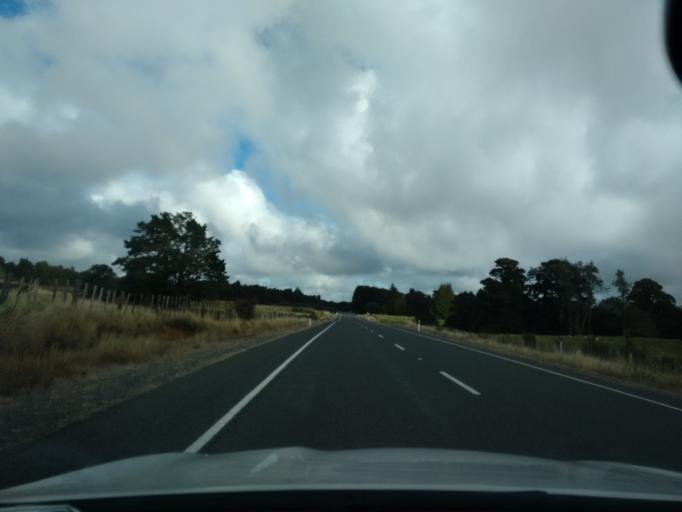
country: NZ
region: Manawatu-Wanganui
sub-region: Ruapehu District
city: Waiouru
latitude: -39.2939
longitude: 175.3878
